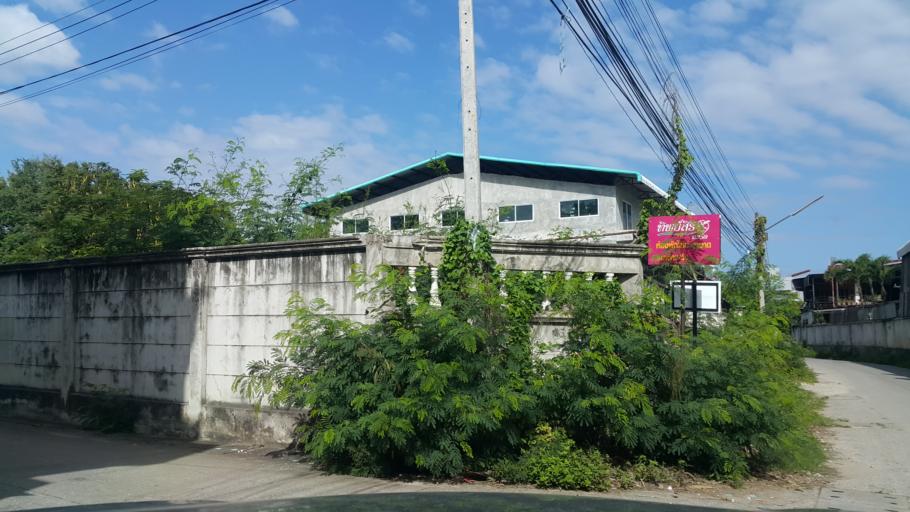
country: TH
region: Chiang Mai
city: Chiang Mai
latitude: 18.7828
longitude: 99.0240
